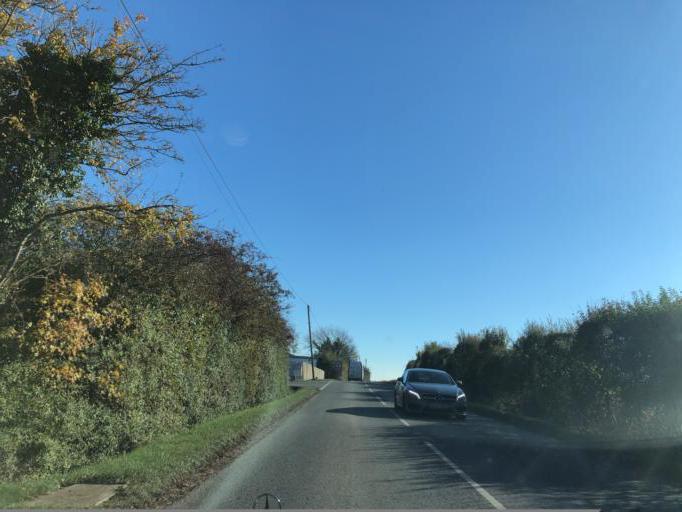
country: GB
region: England
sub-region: Warwickshire
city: Royal Leamington Spa
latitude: 52.2485
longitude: -1.5134
